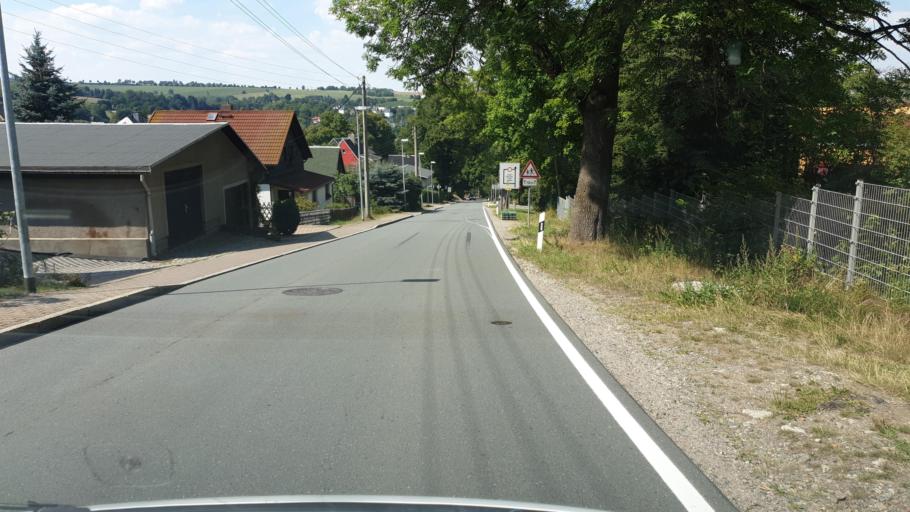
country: DE
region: Saxony
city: Zschopau
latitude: 50.7399
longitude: 13.0710
